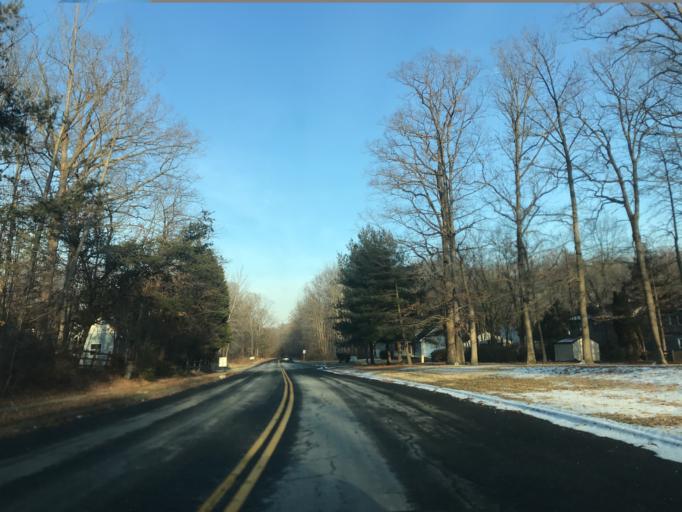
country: US
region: Maryland
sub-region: Harford County
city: Edgewood
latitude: 39.4308
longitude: -76.2664
